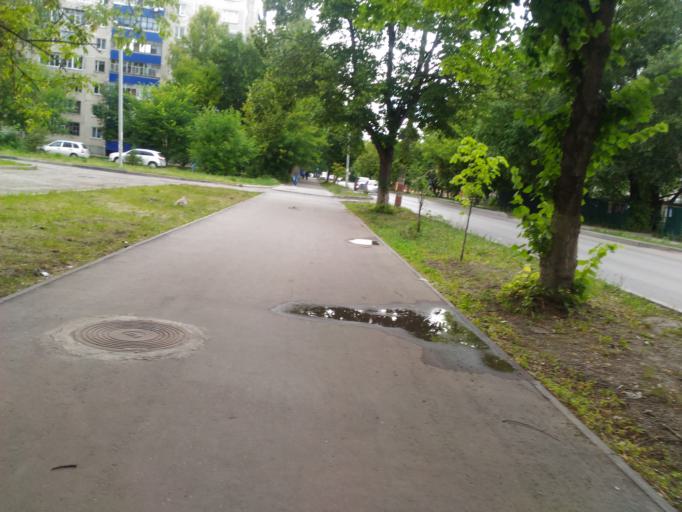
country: RU
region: Ulyanovsk
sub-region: Ulyanovskiy Rayon
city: Ulyanovsk
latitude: 54.2824
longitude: 48.2914
